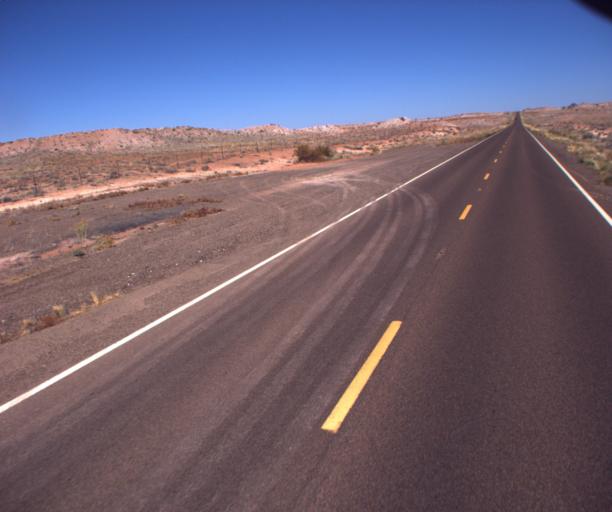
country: US
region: Arizona
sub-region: Navajo County
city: Dilkon
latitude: 35.1948
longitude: -110.4412
